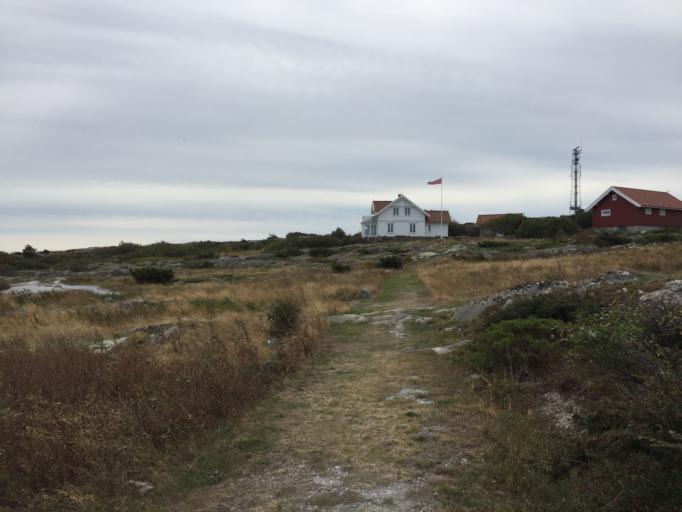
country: NO
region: Ostfold
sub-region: Hvaler
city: Skjaerhalden
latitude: 59.0346
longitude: 10.9468
